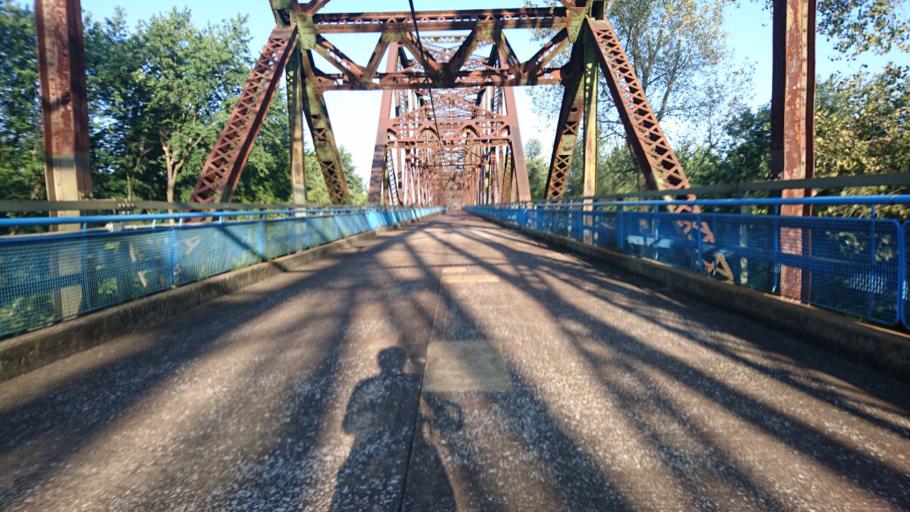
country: US
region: Missouri
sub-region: Saint Louis County
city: Glasgow Village
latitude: 38.7584
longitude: -90.1692
